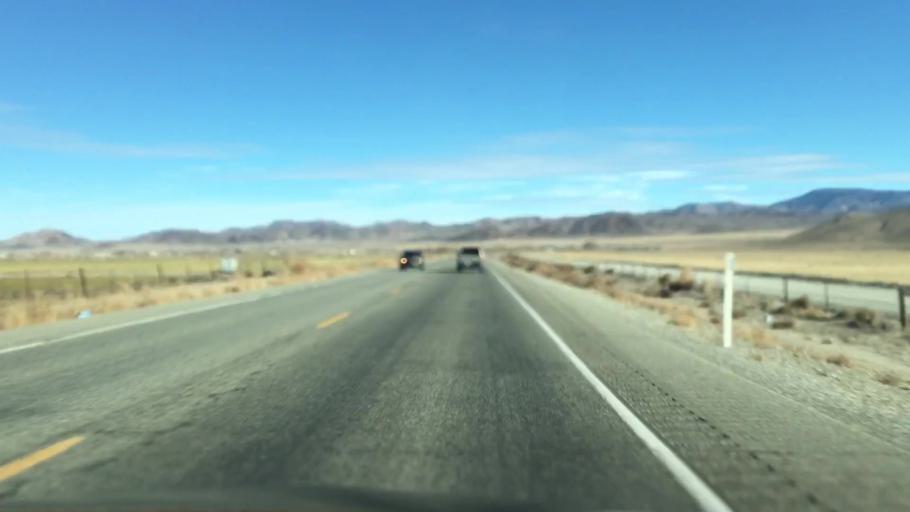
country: US
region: Nevada
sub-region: Lyon County
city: Yerington
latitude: 38.9974
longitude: -119.1120
